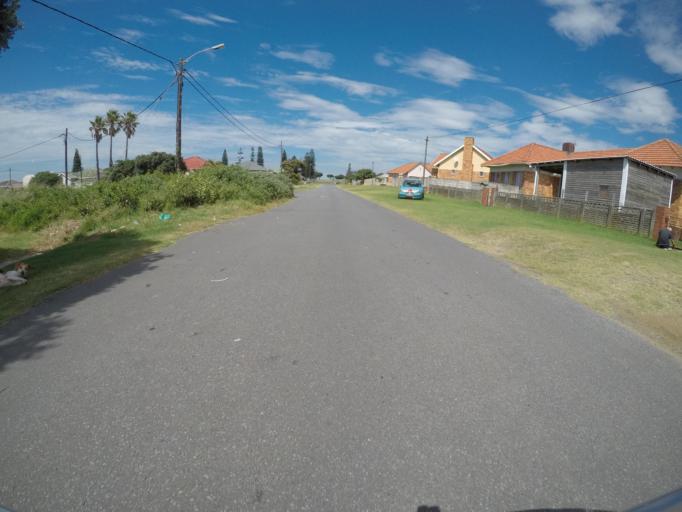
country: ZA
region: Eastern Cape
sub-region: Buffalo City Metropolitan Municipality
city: East London
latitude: -33.0363
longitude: 27.9034
